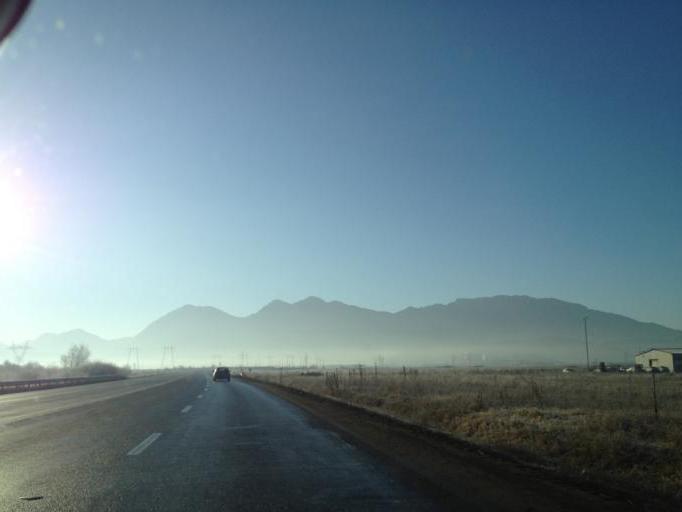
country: RO
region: Brasov
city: Brasov
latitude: 45.6432
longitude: 25.6553
